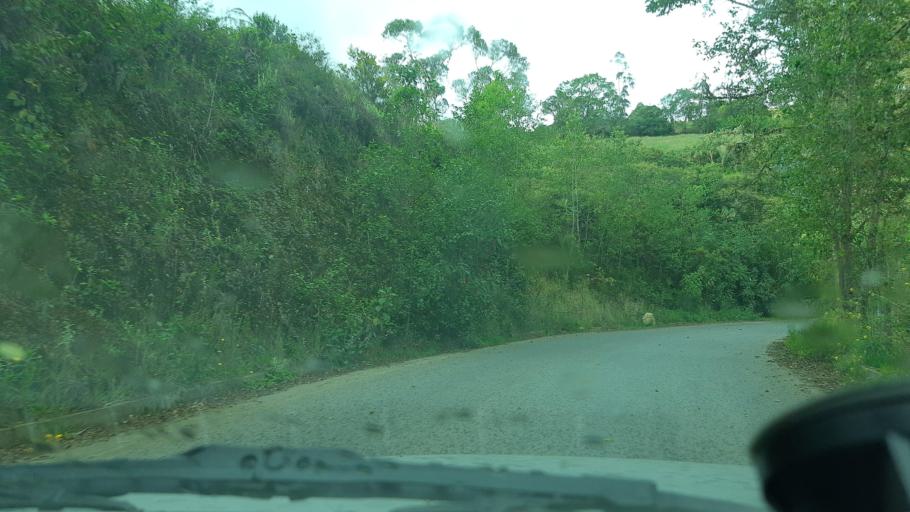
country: CO
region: Cundinamarca
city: Umbita
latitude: 5.2167
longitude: -73.4753
